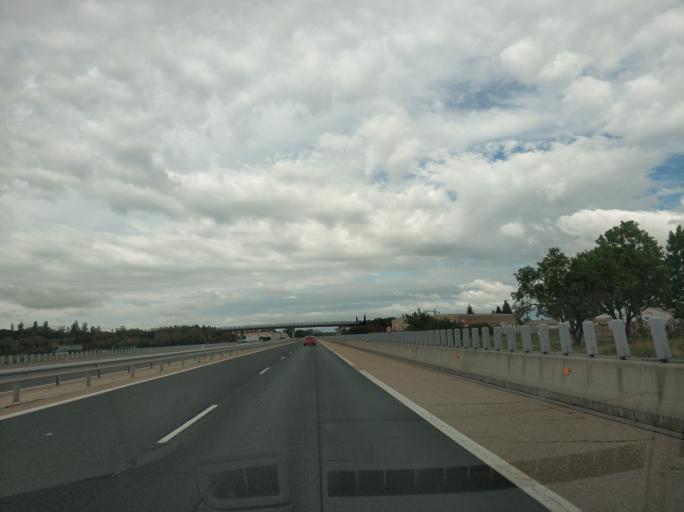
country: ES
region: Castille and Leon
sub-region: Provincia de Valladolid
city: Tudela de Duero
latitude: 41.5925
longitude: -4.5920
